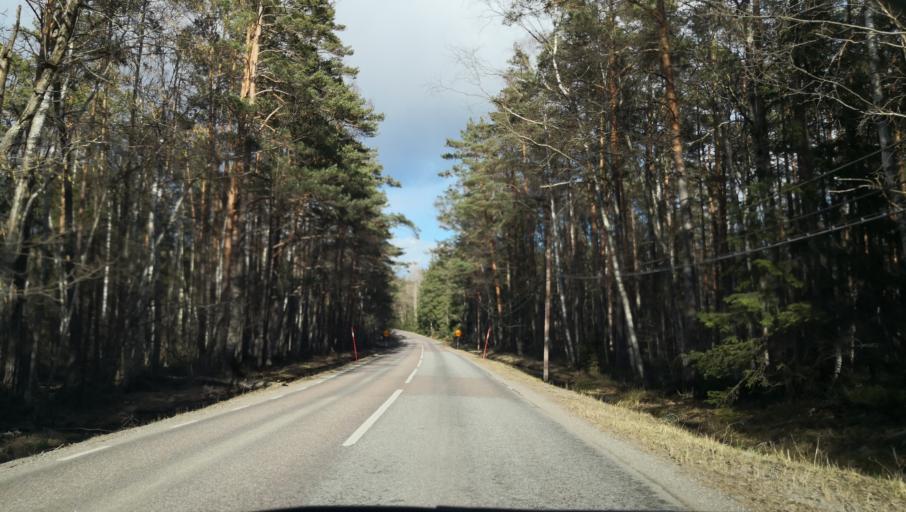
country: SE
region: Stockholm
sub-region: Varmdo Kommun
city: Hemmesta
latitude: 59.2793
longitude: 18.4776
